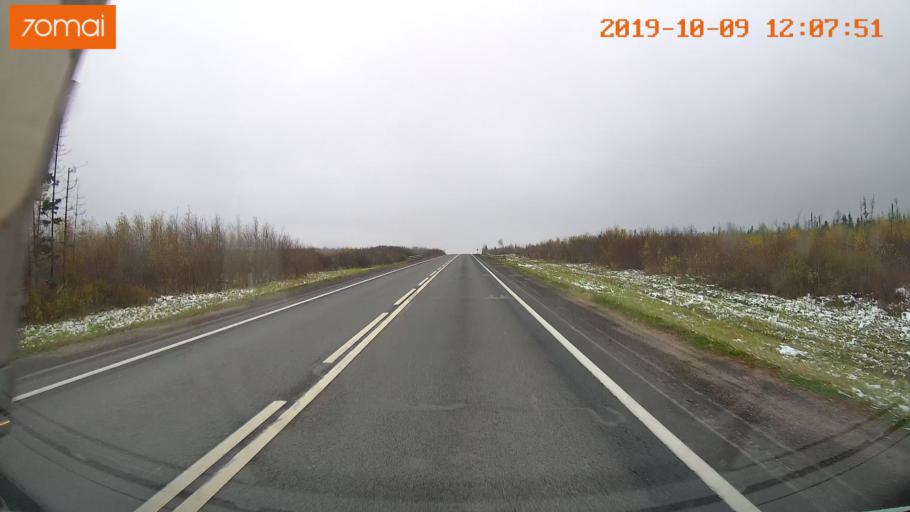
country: RU
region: Jaroslavl
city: Prechistoye
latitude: 58.5942
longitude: 40.3442
